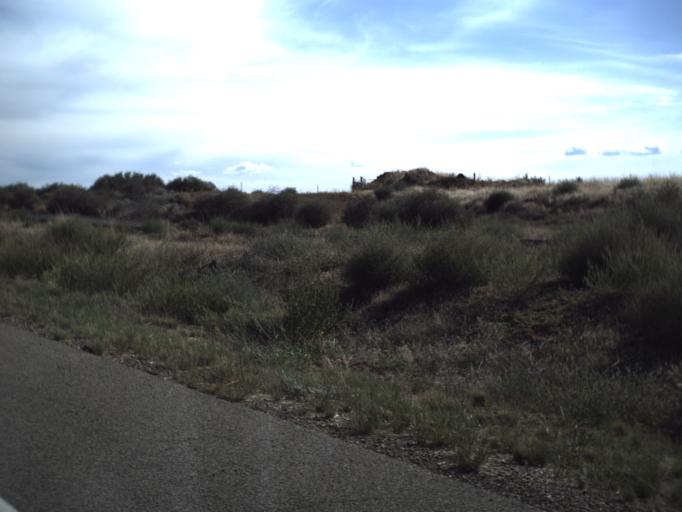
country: US
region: Utah
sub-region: Washington County
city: Ivins
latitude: 37.1915
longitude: -113.6214
